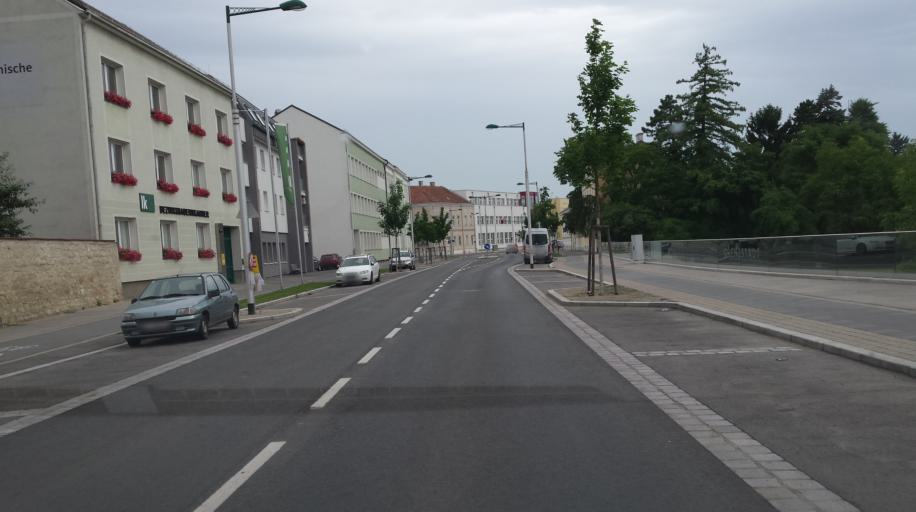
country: AT
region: Burgenland
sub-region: Politischer Bezirk Neusiedl am See
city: Bruckneudorf
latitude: 48.0242
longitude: 16.7754
